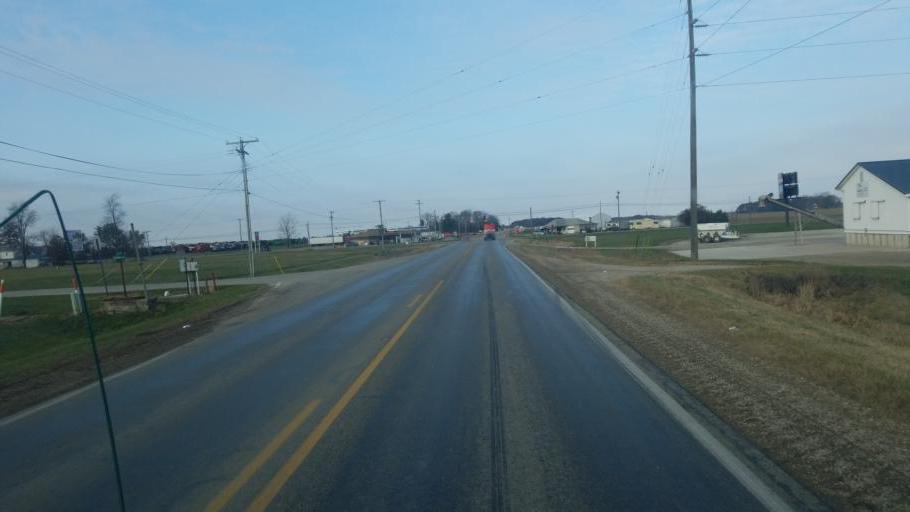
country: US
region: Indiana
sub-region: Adams County
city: Geneva
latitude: 40.5411
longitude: -84.9618
